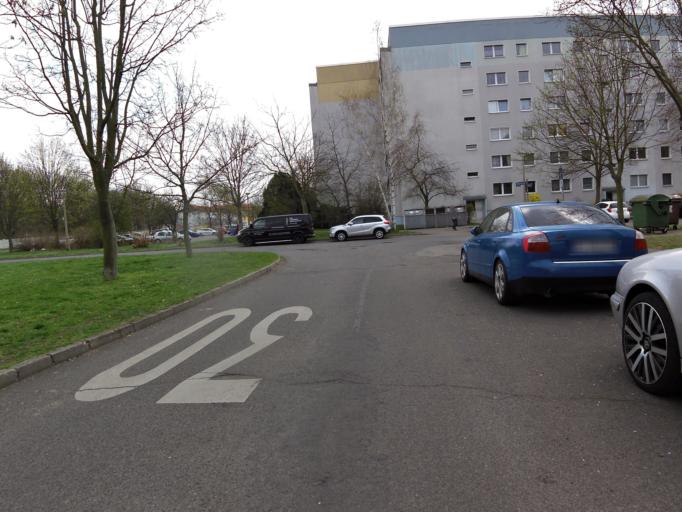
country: DE
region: Saxony
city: Leipzig
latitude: 51.3162
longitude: 12.2987
